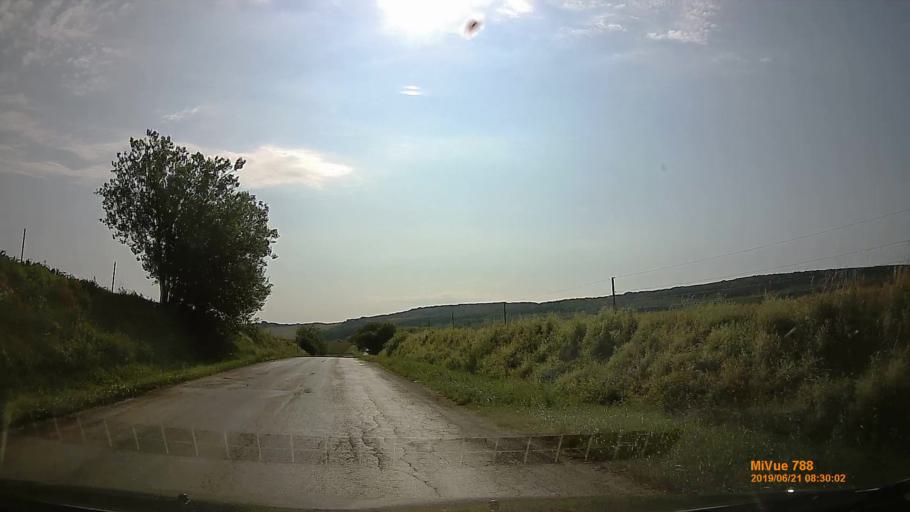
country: HU
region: Baranya
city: Szigetvar
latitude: 46.1467
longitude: 17.8517
